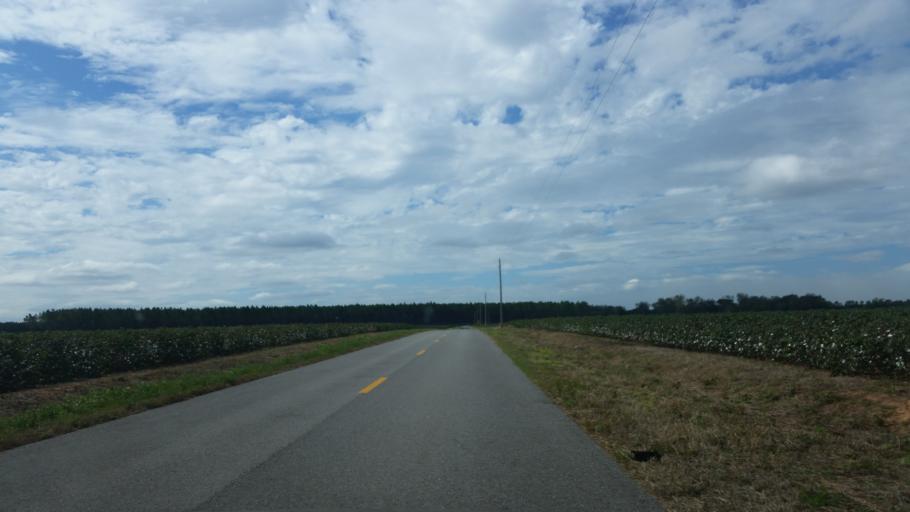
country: US
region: Florida
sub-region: Santa Rosa County
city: Point Baker
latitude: 30.7366
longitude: -87.0249
